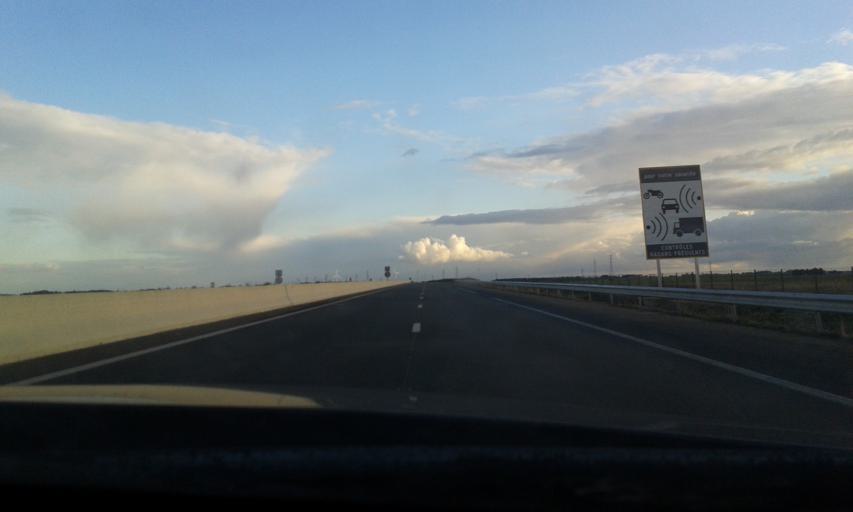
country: FR
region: Centre
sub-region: Departement d'Eure-et-Loir
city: Sours
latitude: 48.3724
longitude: 1.5894
